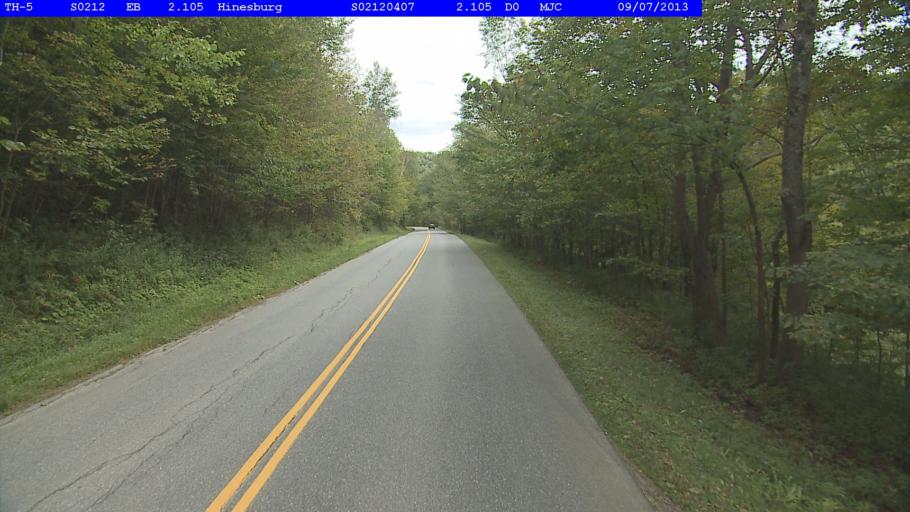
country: US
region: Vermont
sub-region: Chittenden County
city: Hinesburg
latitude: 44.2882
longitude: -73.0302
